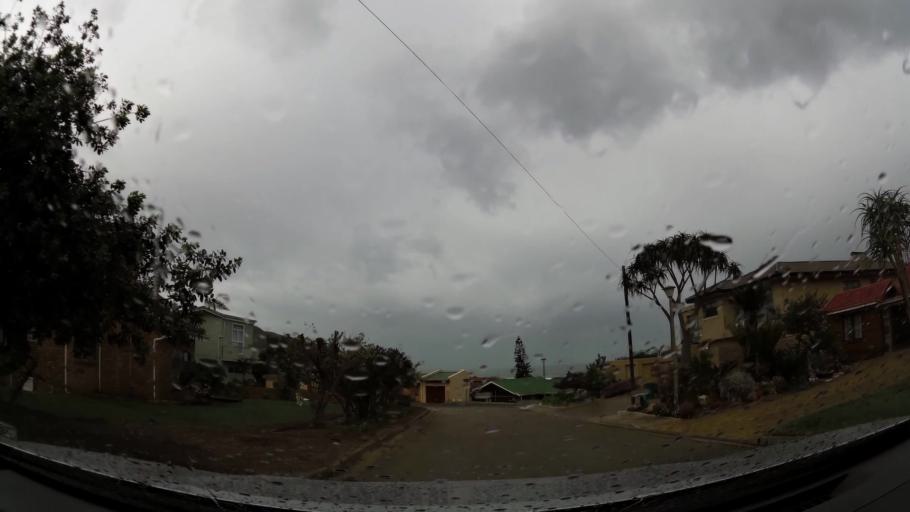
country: ZA
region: Western Cape
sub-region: Eden District Municipality
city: George
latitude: -34.0482
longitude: 22.3105
